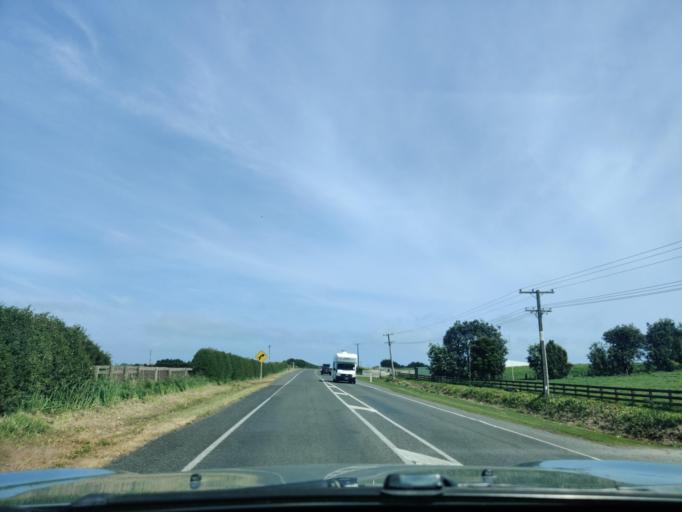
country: NZ
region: Taranaki
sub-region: South Taranaki District
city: Patea
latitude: -39.7153
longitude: 174.4485
